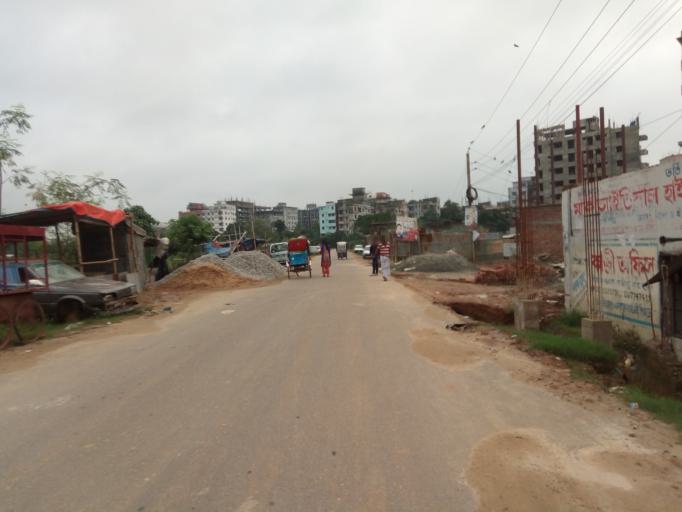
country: BD
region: Dhaka
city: Tungi
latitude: 23.8493
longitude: 90.4165
